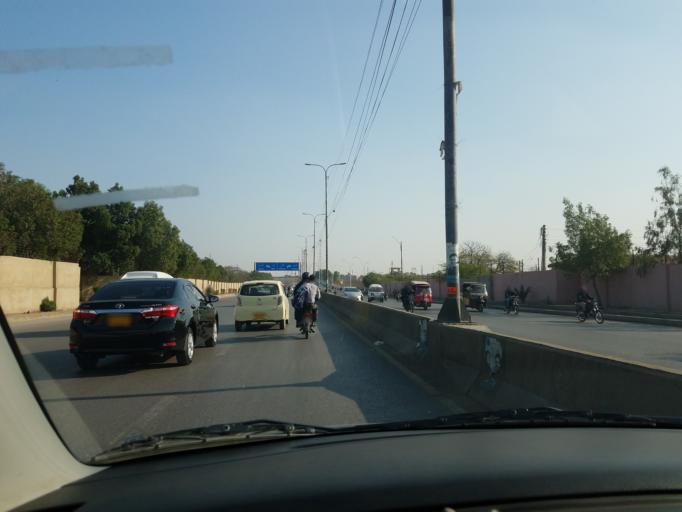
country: PK
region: Sindh
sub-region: Karachi District
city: Karachi
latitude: 24.8907
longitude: 67.1229
